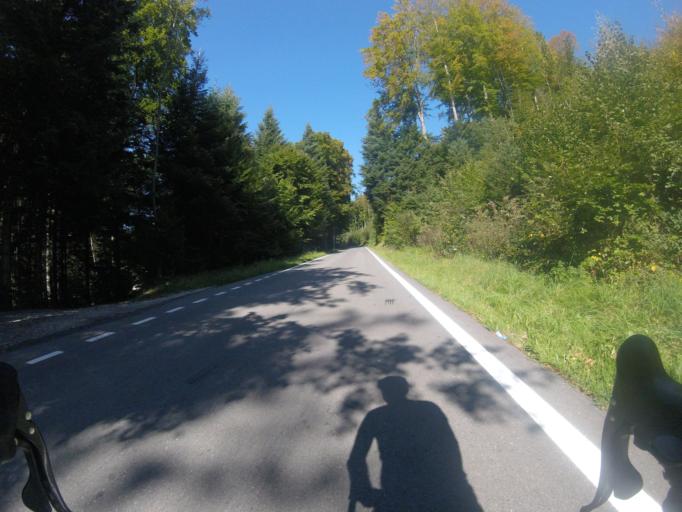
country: CH
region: Bern
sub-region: Bern-Mittelland District
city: Toffen
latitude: 46.8669
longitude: 7.5125
